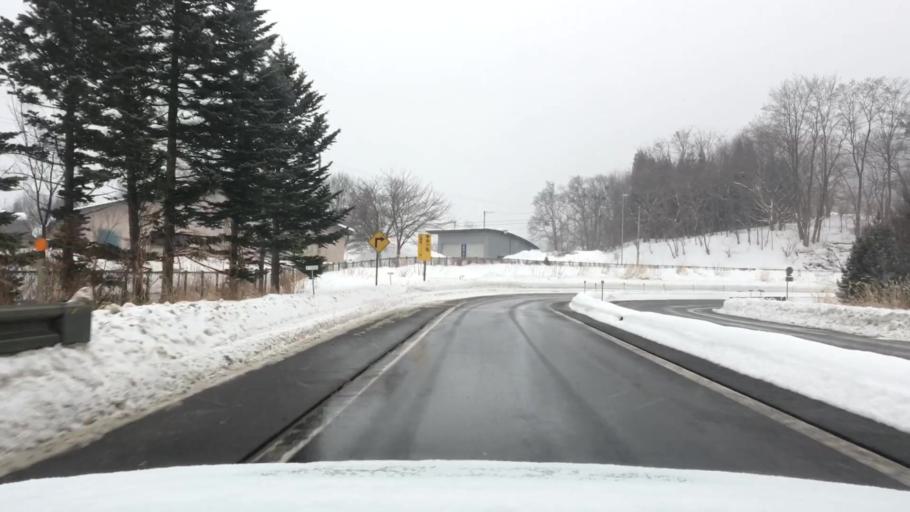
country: JP
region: Iwate
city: Ichinohe
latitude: 40.1091
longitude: 141.0486
